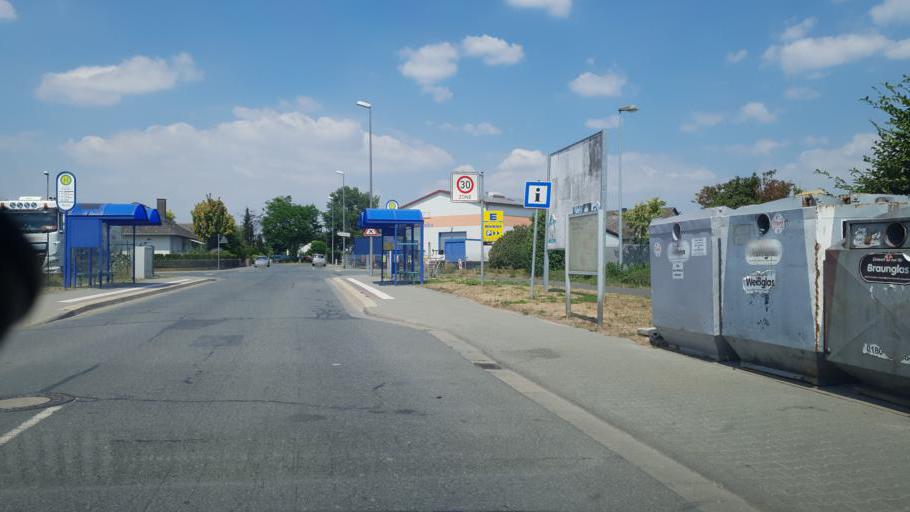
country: DE
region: Hesse
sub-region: Regierungsbezirk Darmstadt
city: Buttelborn
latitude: 49.9210
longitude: 8.5283
